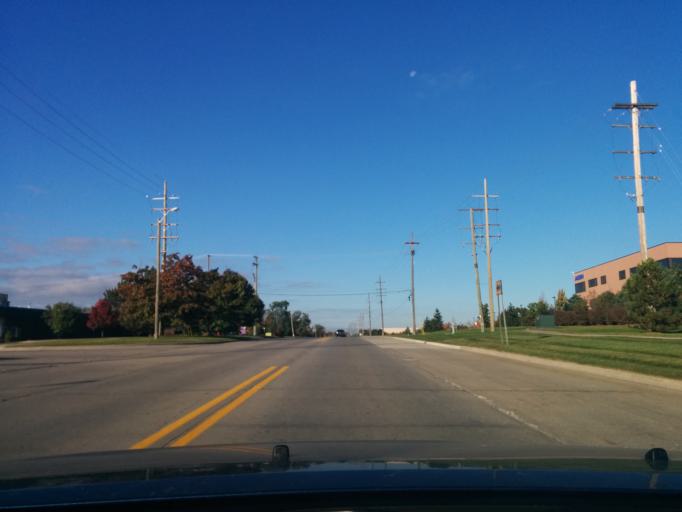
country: US
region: Michigan
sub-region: Wayne County
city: Plymouth
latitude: 42.3951
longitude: -83.4962
